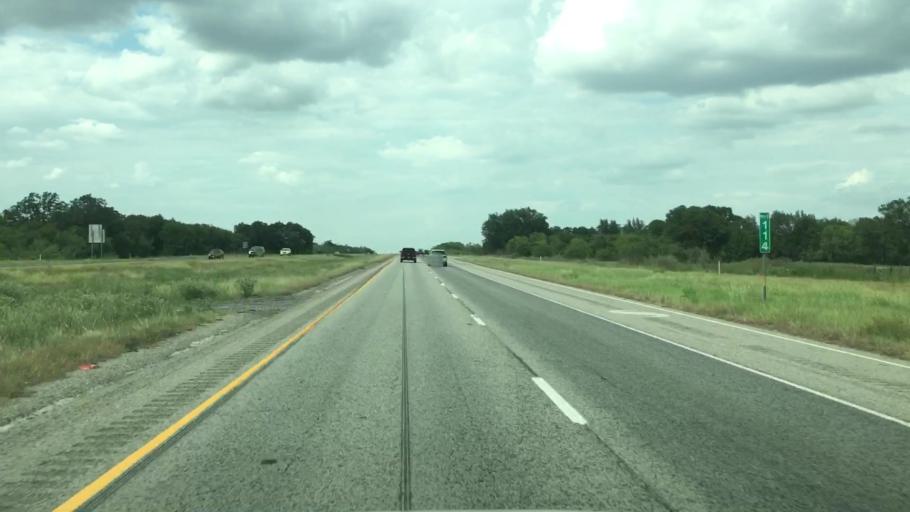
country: US
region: Texas
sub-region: Atascosa County
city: Pleasanton
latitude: 29.0541
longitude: -98.4321
